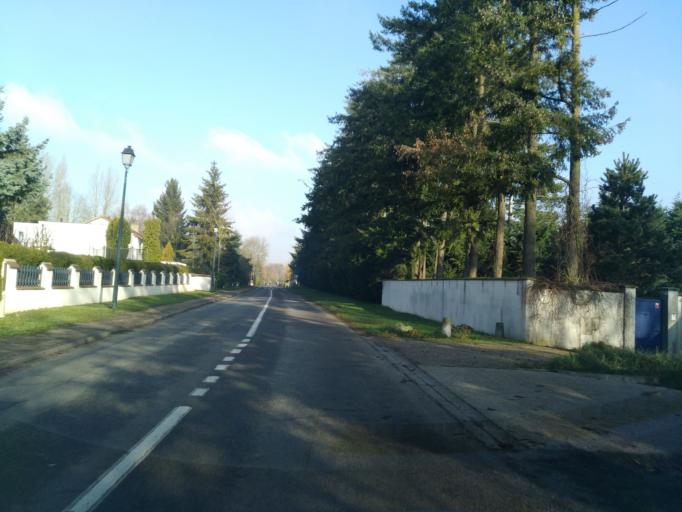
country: FR
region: Ile-de-France
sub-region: Departement des Yvelines
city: Feucherolles
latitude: 48.8779
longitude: 1.9798
